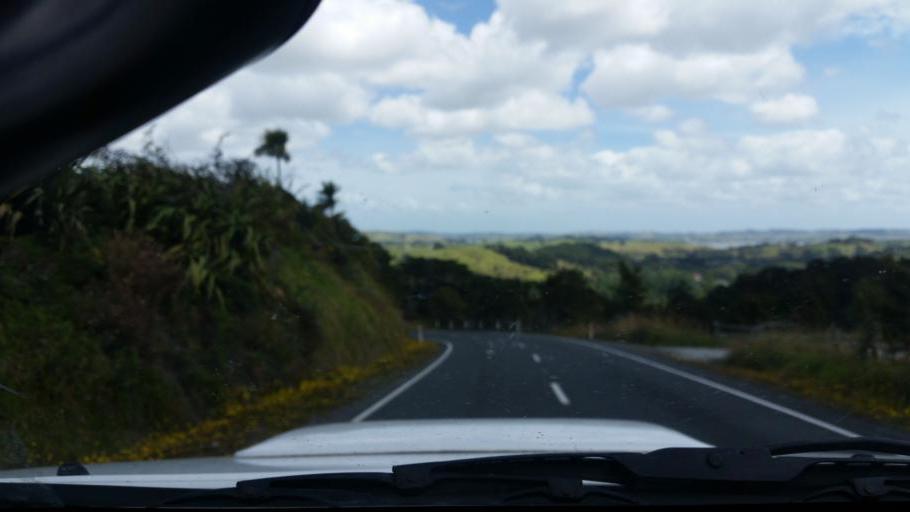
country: NZ
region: Northland
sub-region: Whangarei
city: Ruakaka
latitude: -36.0881
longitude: 174.2396
